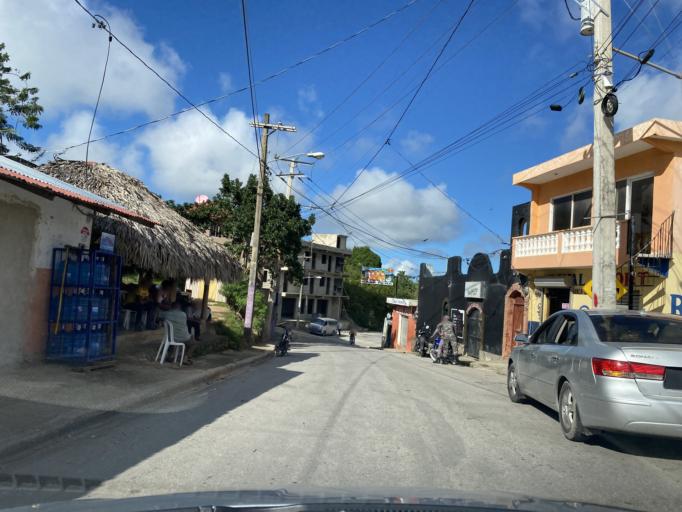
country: DO
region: Samana
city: Sanchez
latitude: 19.2583
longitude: -69.5706
